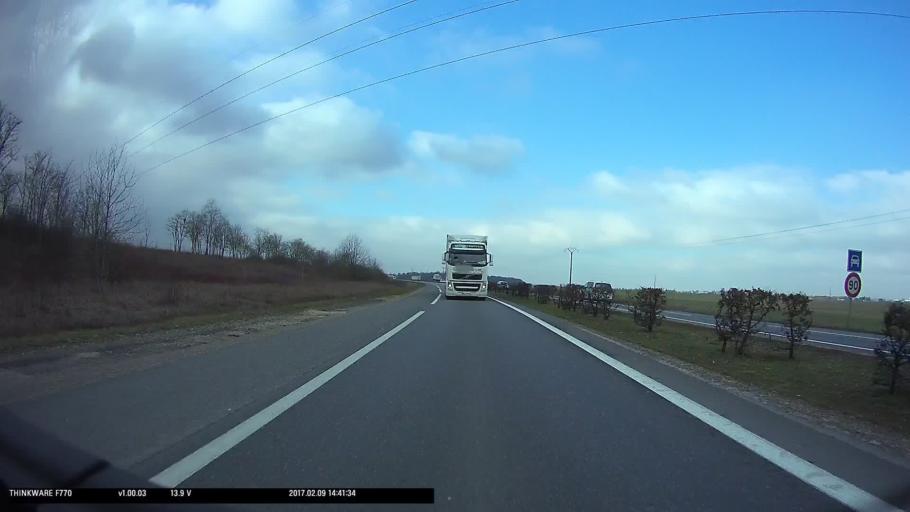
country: FR
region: Centre
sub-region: Departement du Cher
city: Trouy
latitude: 47.0342
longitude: 2.3724
